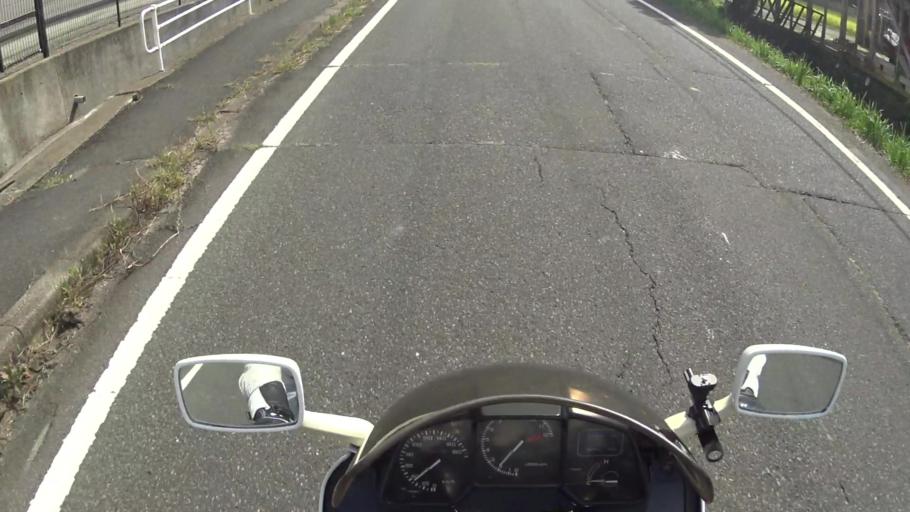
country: JP
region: Kyoto
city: Miyazu
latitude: 35.6497
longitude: 135.0917
